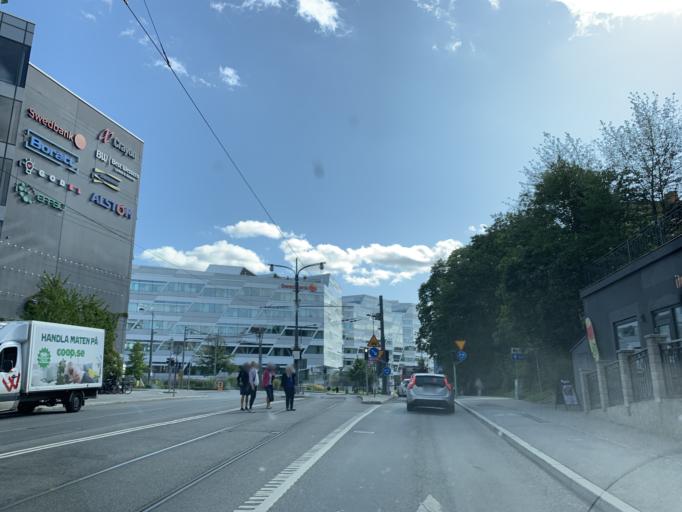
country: SE
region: Stockholm
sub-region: Sundbybergs Kommun
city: Sundbyberg
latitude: 59.3600
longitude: 17.9721
